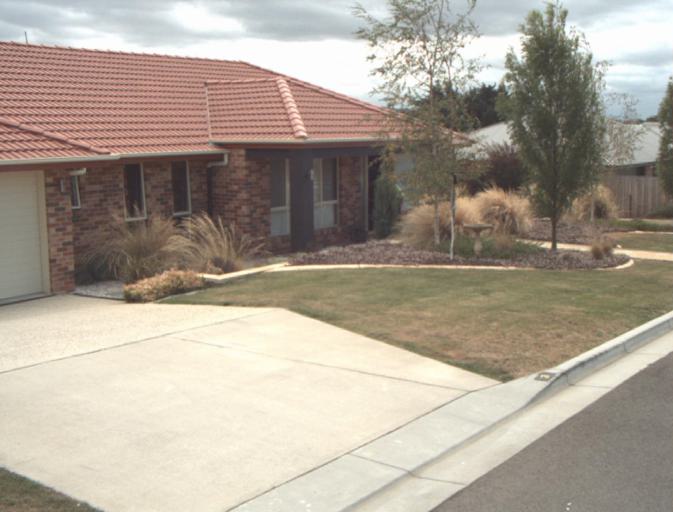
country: AU
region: Tasmania
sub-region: Launceston
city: Newstead
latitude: -41.4597
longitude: 147.1980
